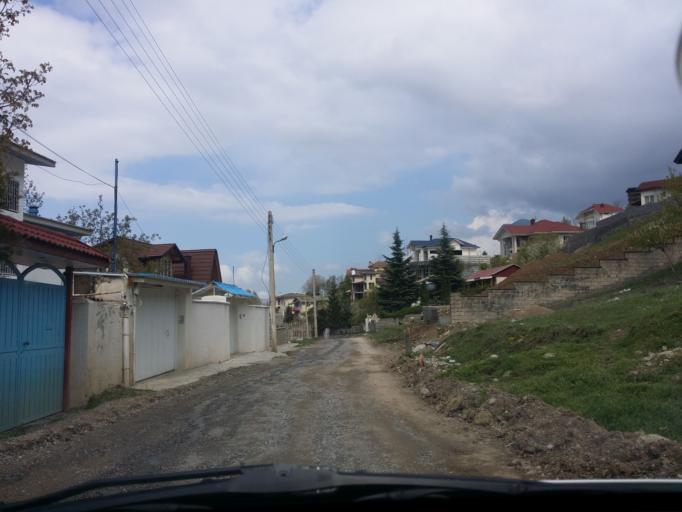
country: IR
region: Mazandaran
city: `Abbasabad
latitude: 36.4866
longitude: 51.1419
